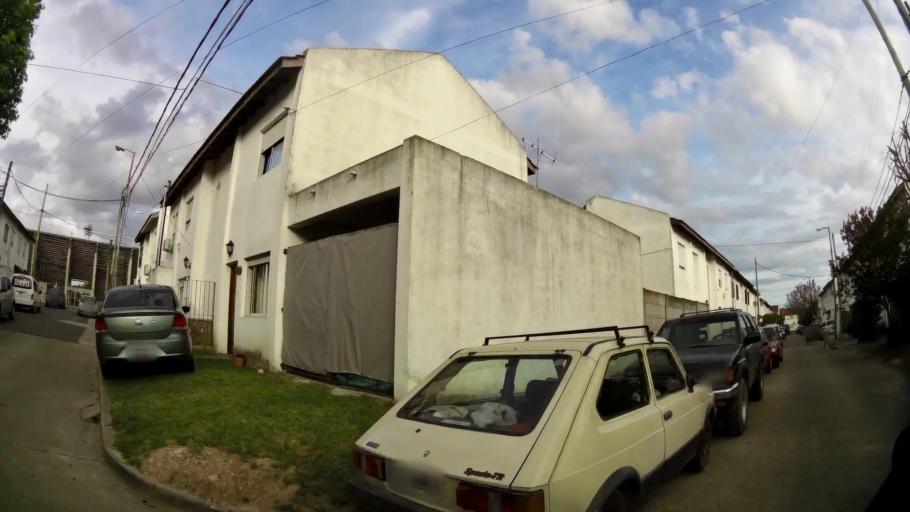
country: AR
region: Buenos Aires
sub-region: Partido de Quilmes
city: Quilmes
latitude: -34.7435
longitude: -58.2537
